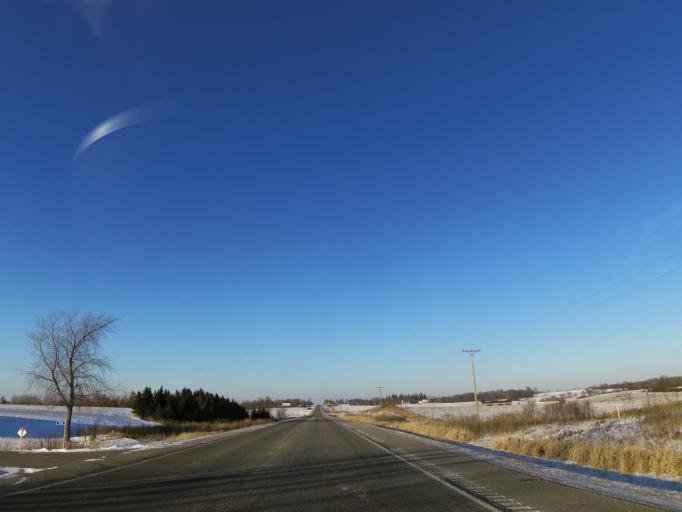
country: US
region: Minnesota
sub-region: Rice County
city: Lonsdale
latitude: 44.5059
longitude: -93.4433
